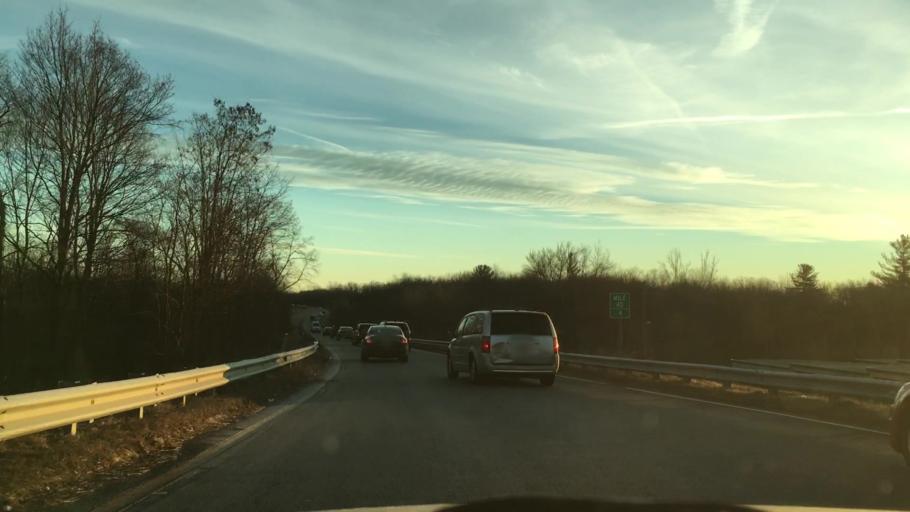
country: US
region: Massachusetts
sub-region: Hampden County
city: Agawam
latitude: 42.0551
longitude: -72.6750
